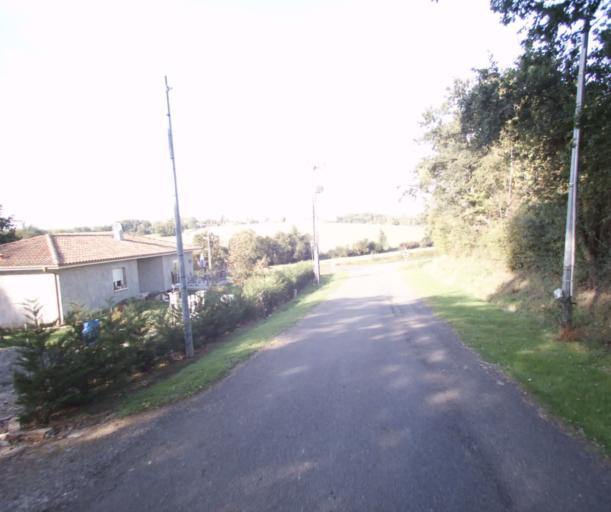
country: FR
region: Midi-Pyrenees
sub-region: Departement du Gers
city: Eauze
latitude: 43.8584
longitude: 0.0414
